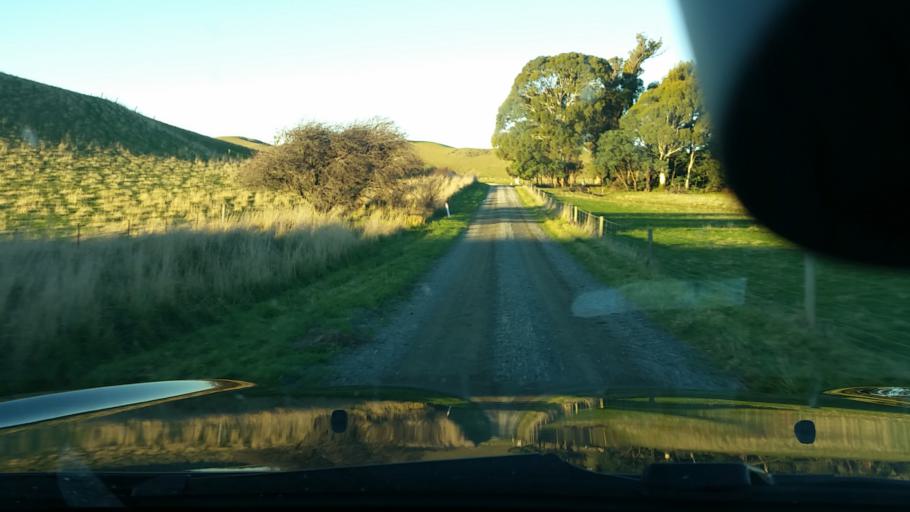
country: NZ
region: Marlborough
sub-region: Marlborough District
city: Blenheim
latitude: -41.7488
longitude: 174.0724
